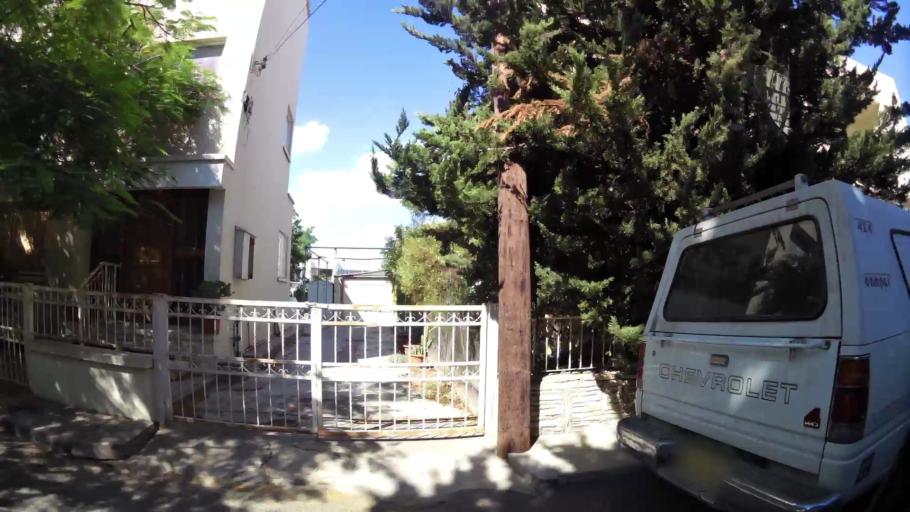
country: CY
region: Larnaka
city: Larnaca
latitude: 34.9209
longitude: 33.6349
